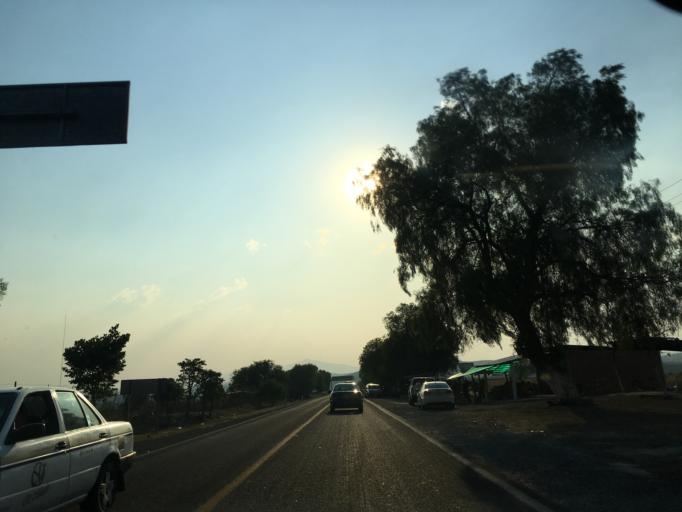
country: MX
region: Michoacan
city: Charo
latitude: 19.7466
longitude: -101.0545
